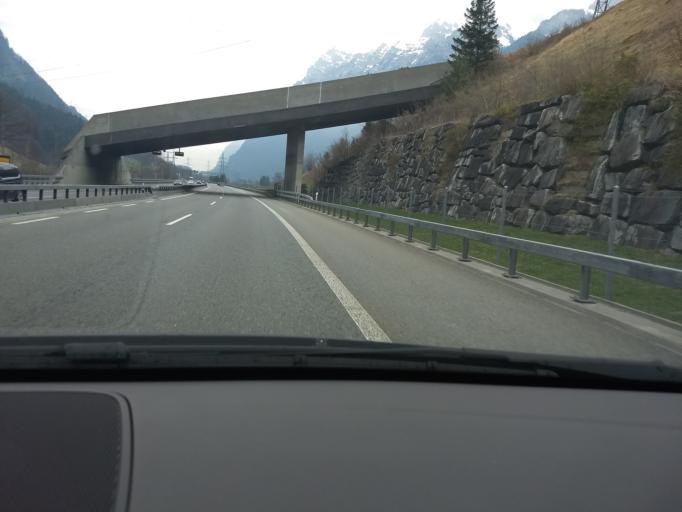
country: CH
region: Uri
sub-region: Uri
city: Silenen
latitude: 46.7839
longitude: 8.6734
